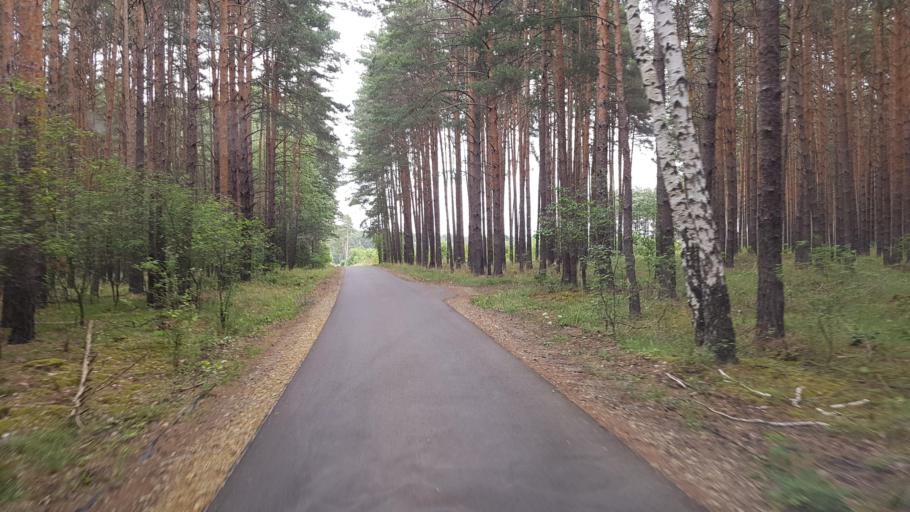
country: DE
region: Brandenburg
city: Grossraschen
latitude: 51.6042
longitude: 14.0391
